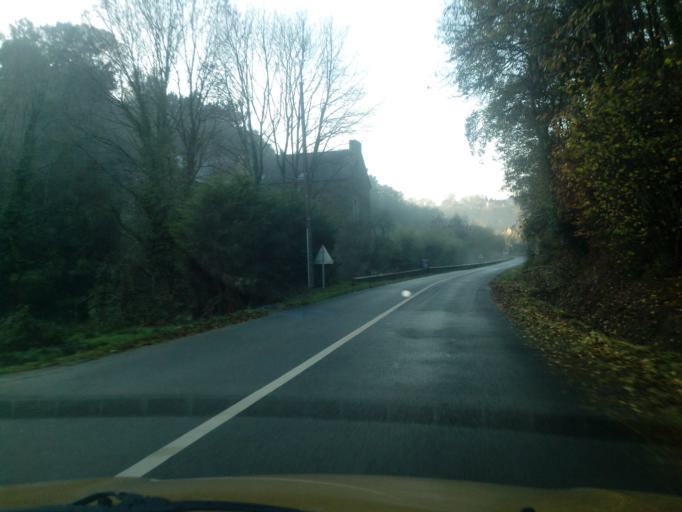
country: FR
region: Brittany
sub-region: Departement du Morbihan
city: Pluherlin
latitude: 47.7054
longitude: -2.3360
